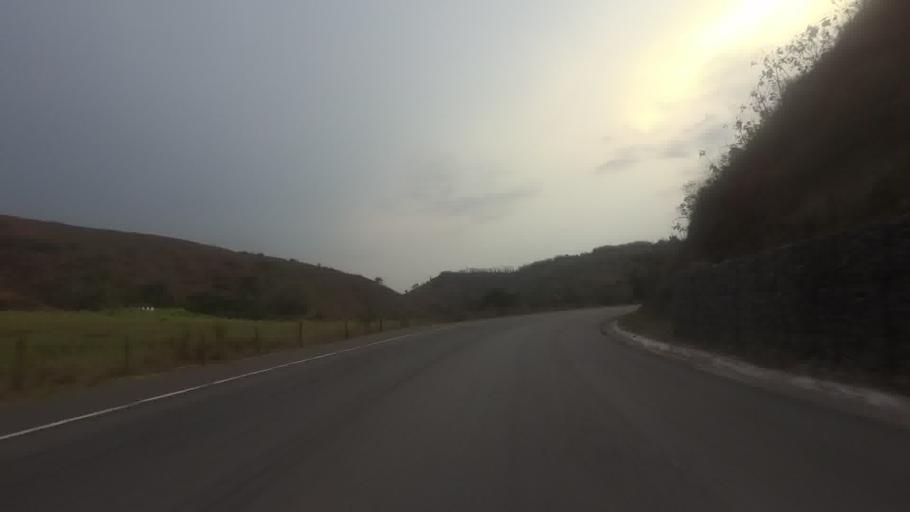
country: BR
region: Minas Gerais
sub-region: Alem Paraiba
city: Alem Paraiba
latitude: -21.8492
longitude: -42.6400
